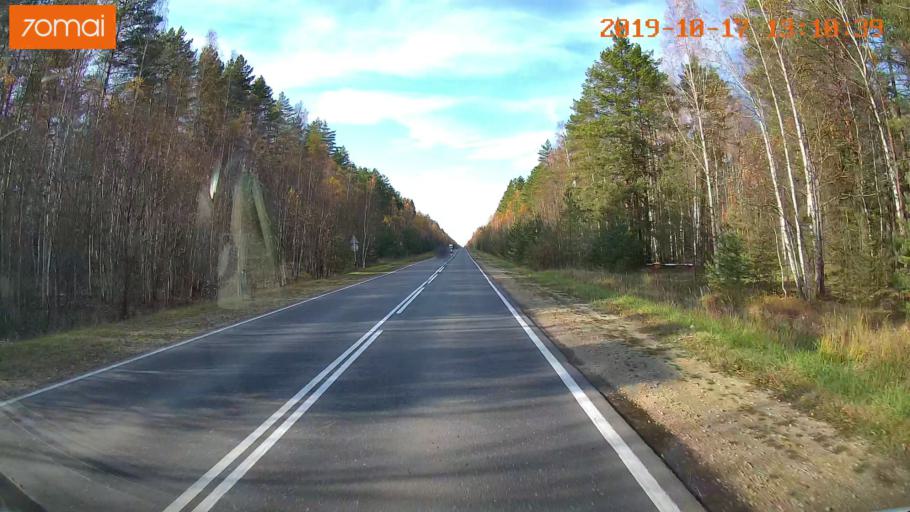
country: RU
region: Rjazan
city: Syntul
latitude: 55.0209
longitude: 41.2528
